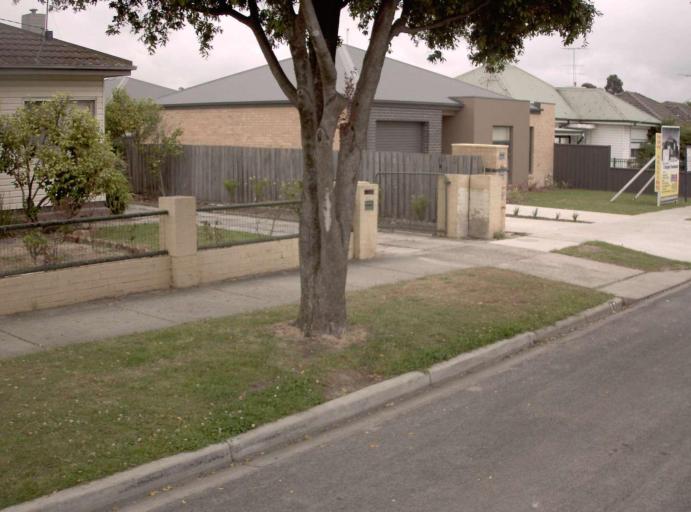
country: AU
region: Victoria
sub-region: Latrobe
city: Morwell
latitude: -38.2370
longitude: 146.4053
